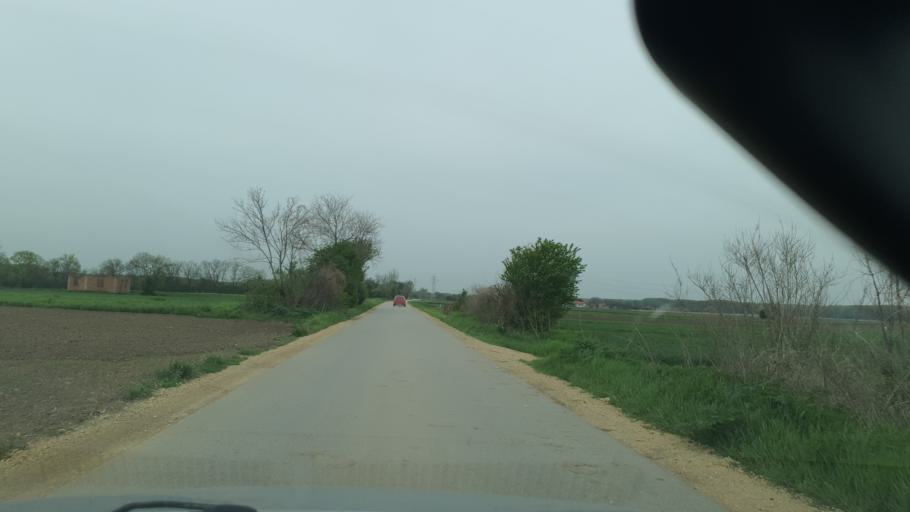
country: RS
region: Central Serbia
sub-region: Branicevski Okrug
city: Pozarevac
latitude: 44.7125
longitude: 21.1343
